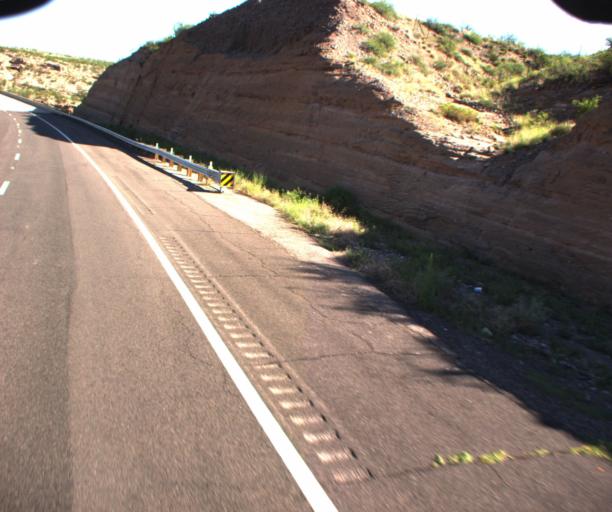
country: US
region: Arizona
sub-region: Greenlee County
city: Clifton
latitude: 32.9528
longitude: -109.2290
